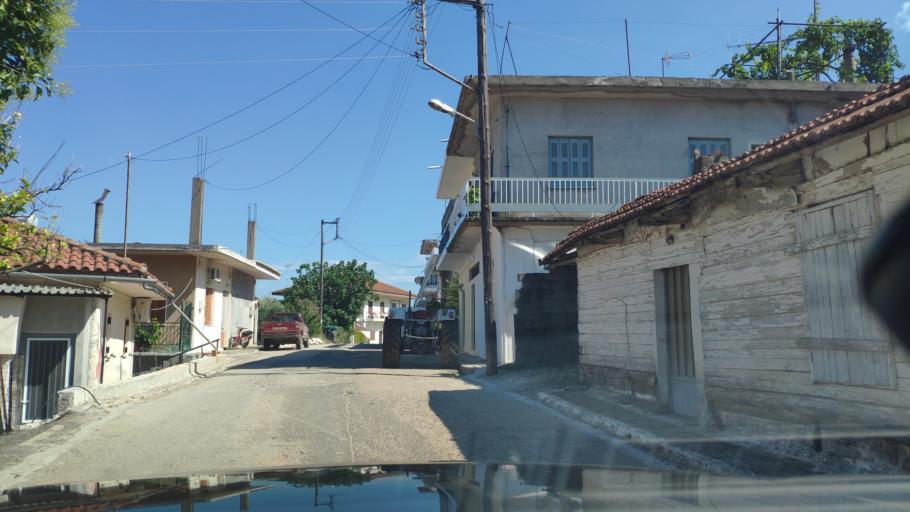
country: GR
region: West Greece
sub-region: Nomos Aitolias kai Akarnanias
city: Katouna
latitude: 38.7884
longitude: 21.1156
